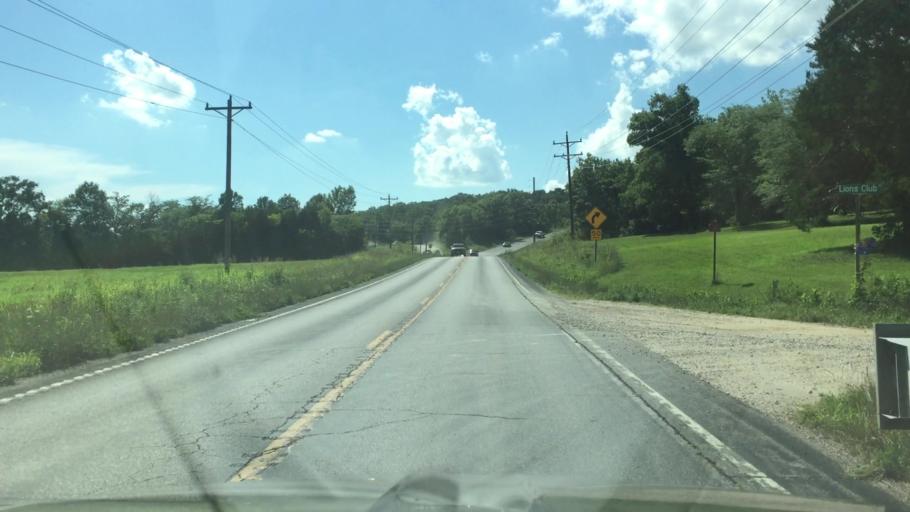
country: US
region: Missouri
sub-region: Miller County
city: Tuscumbia
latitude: 38.0859
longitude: -92.4926
